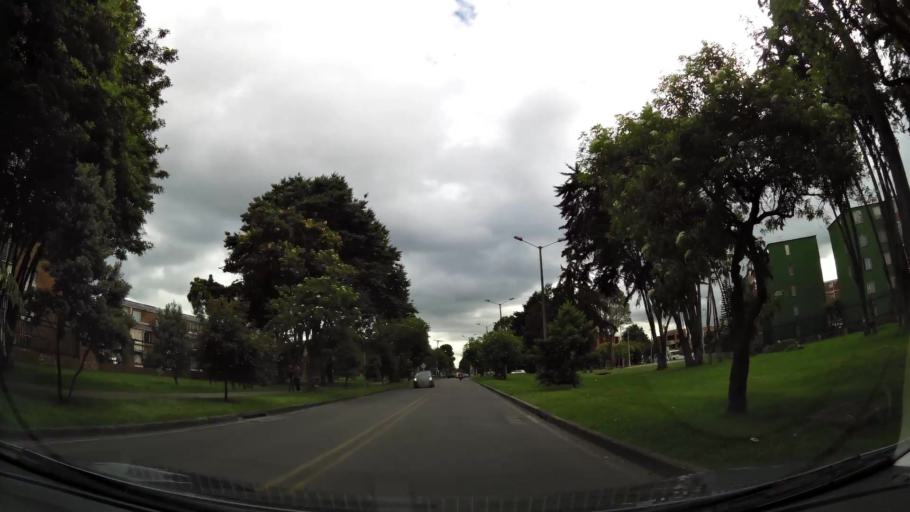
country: CO
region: Cundinamarca
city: Cota
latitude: 4.7193
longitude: -74.1117
